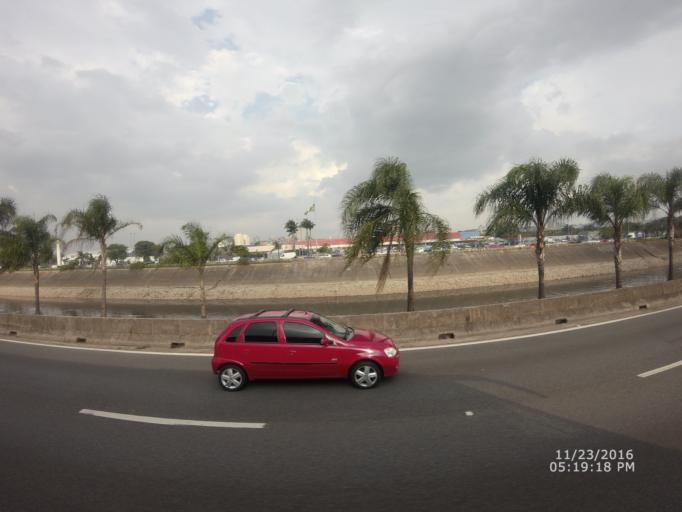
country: BR
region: Sao Paulo
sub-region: Guarulhos
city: Guarulhos
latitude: -23.5122
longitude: -46.5567
